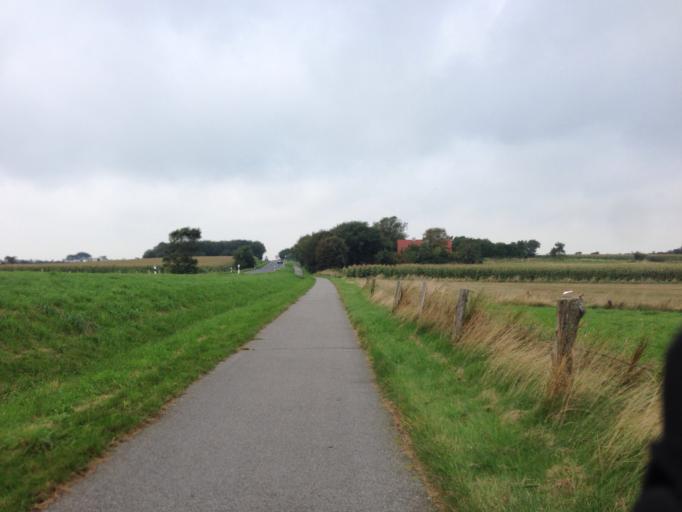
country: DE
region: Schleswig-Holstein
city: Oevenum
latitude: 54.7043
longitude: 8.5368
